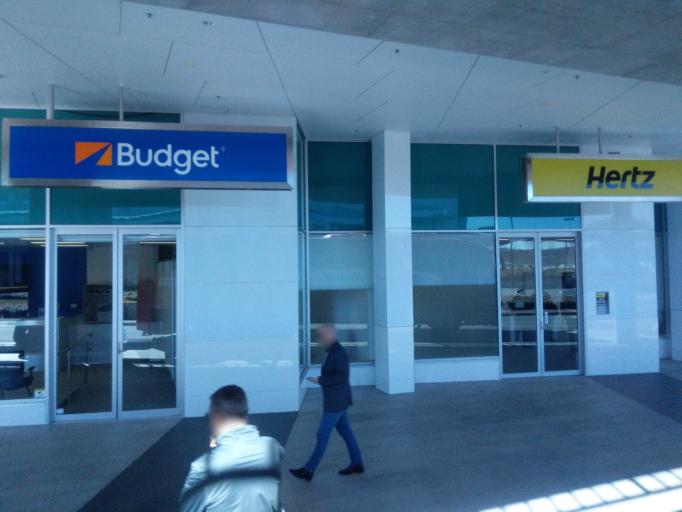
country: AU
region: Australian Capital Territory
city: Forrest
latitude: -35.3082
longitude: 149.1894
